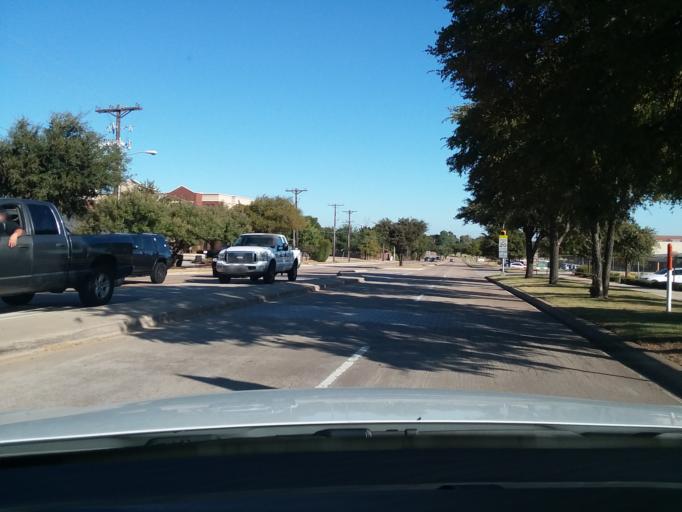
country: US
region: Texas
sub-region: Denton County
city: Highland Village
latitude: 33.0739
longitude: -97.0675
